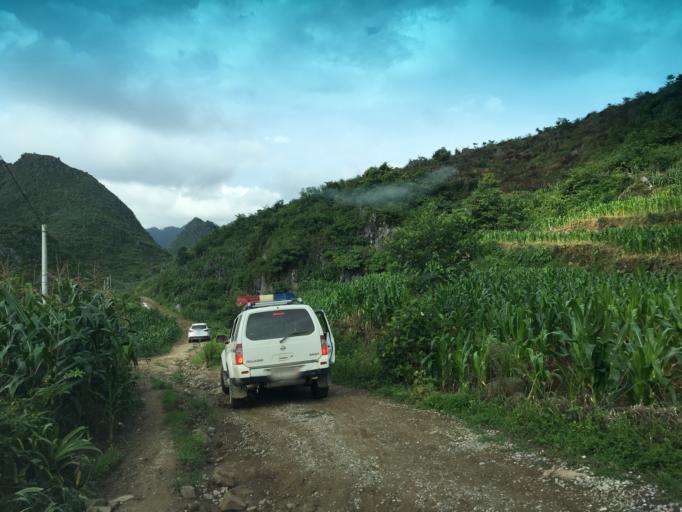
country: CN
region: Guangxi Zhuangzu Zizhiqu
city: Xinzhou
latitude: 24.9905
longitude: 105.6328
